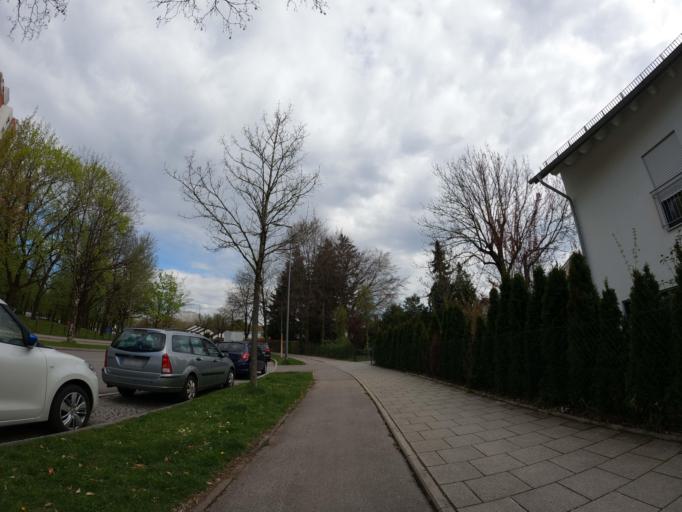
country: DE
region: Bavaria
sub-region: Upper Bavaria
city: Neubiberg
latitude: 48.0998
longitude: 11.6391
